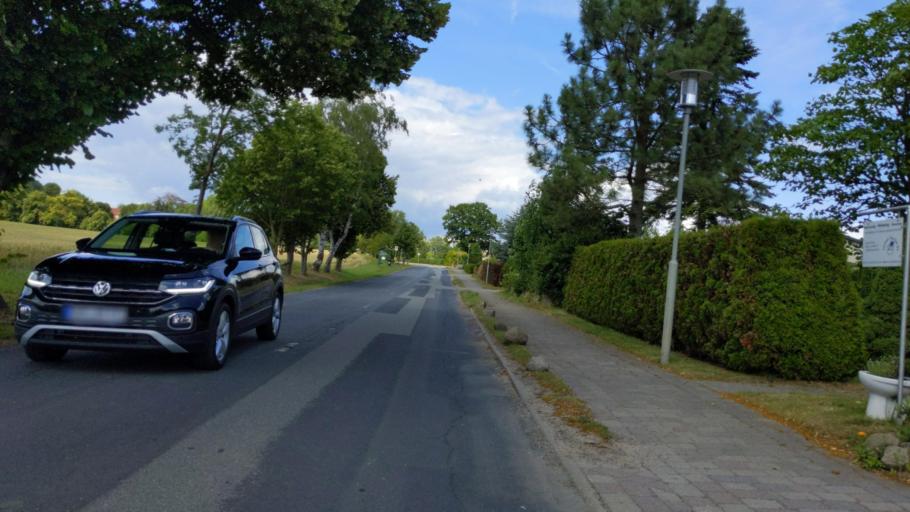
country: DE
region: Mecklenburg-Vorpommern
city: Klutz
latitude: 53.9912
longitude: 11.1250
